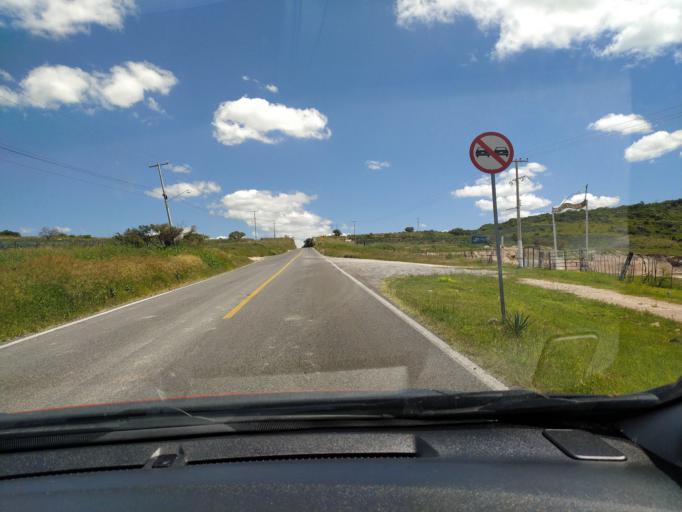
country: MX
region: Jalisco
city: San Diego de Alejandria
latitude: 21.0272
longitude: -101.9306
